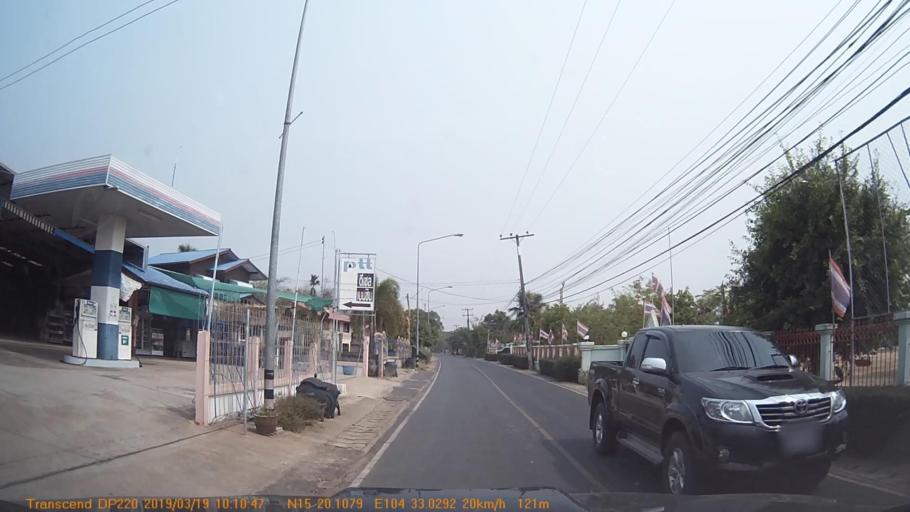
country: TH
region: Changwat Ubon Ratchathani
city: Khueang Nai
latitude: 15.3352
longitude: 104.5505
